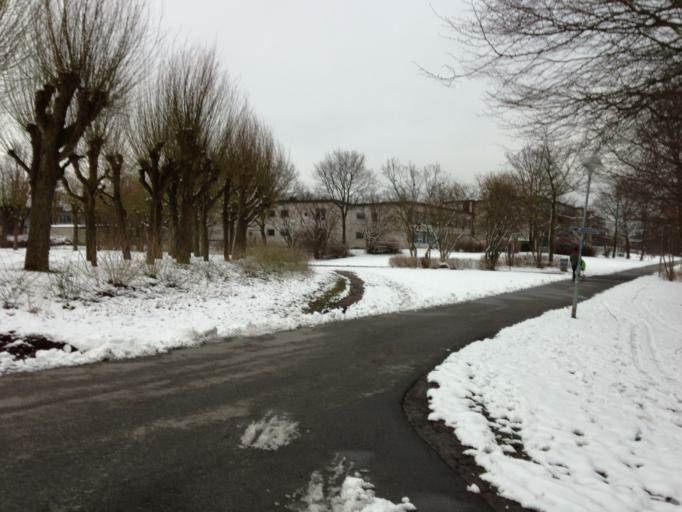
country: SE
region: Skane
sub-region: Lunds Kommun
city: Lund
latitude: 55.7237
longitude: 13.2136
